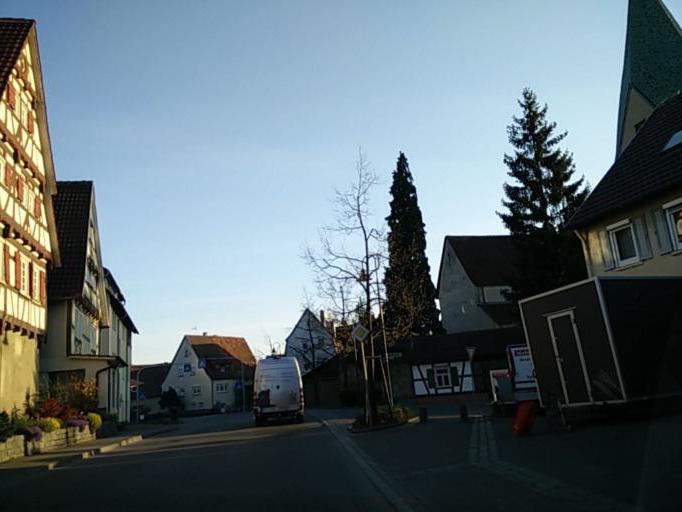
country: DE
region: Baden-Wuerttemberg
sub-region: Regierungsbezirk Stuttgart
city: Hildrizhausen
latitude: 48.6249
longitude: 8.9662
